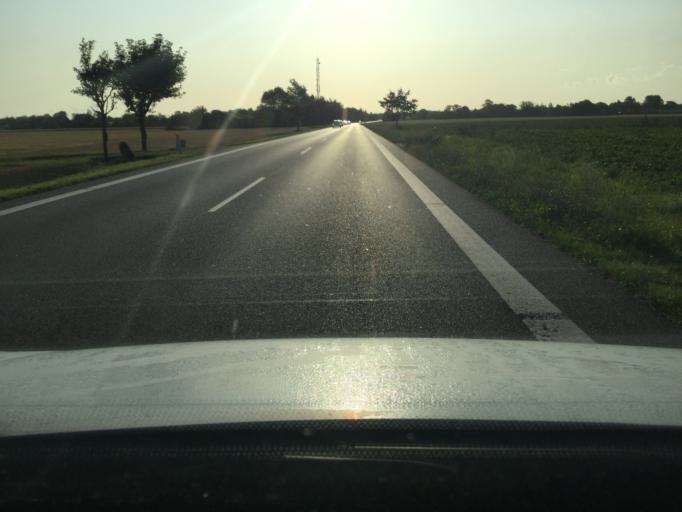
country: DK
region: Zealand
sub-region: Lolland Kommune
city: Nakskov
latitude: 54.8028
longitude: 11.2607
